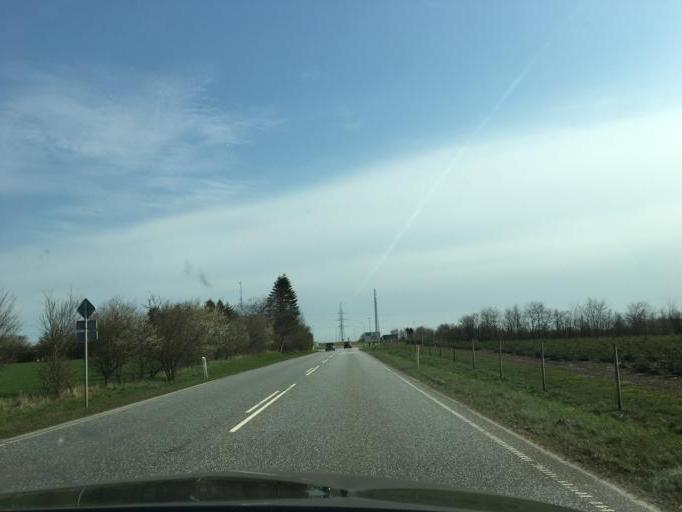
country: DK
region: South Denmark
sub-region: Kolding Kommune
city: Lunderskov
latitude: 55.5040
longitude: 9.3223
